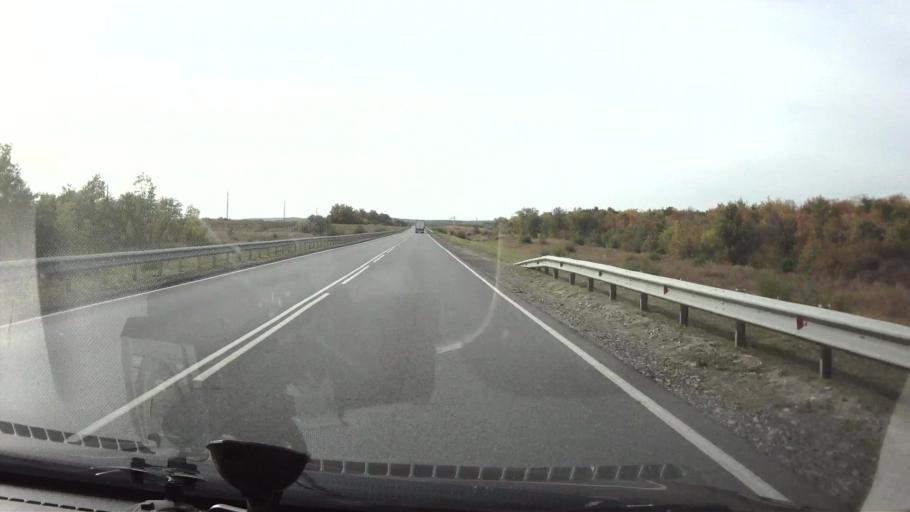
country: RU
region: Saratov
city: Tersa
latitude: 52.0849
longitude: 47.6507
